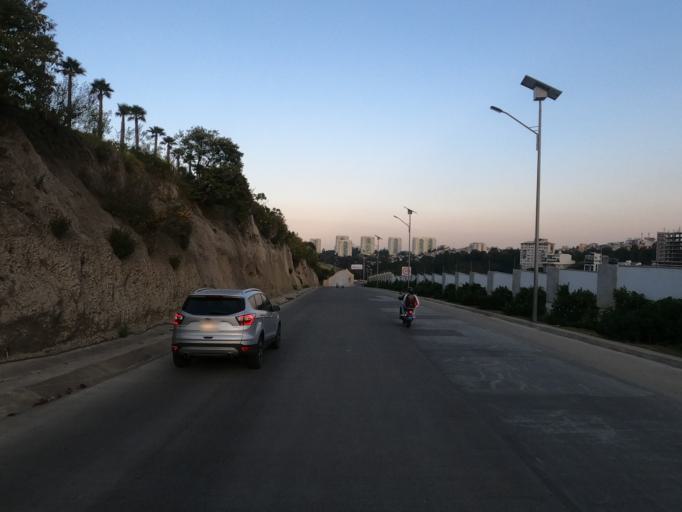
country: MX
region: Mexico
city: San Bartolome Coatepec
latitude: 19.4128
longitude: -99.2904
